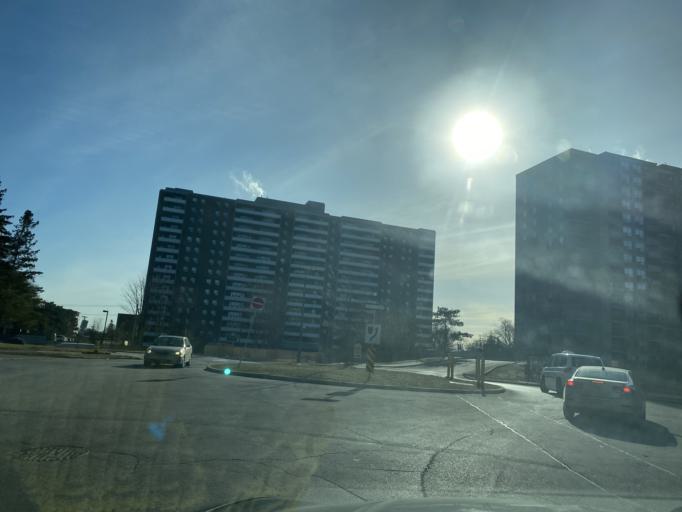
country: CA
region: Ontario
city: Scarborough
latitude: 43.7833
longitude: -79.2968
